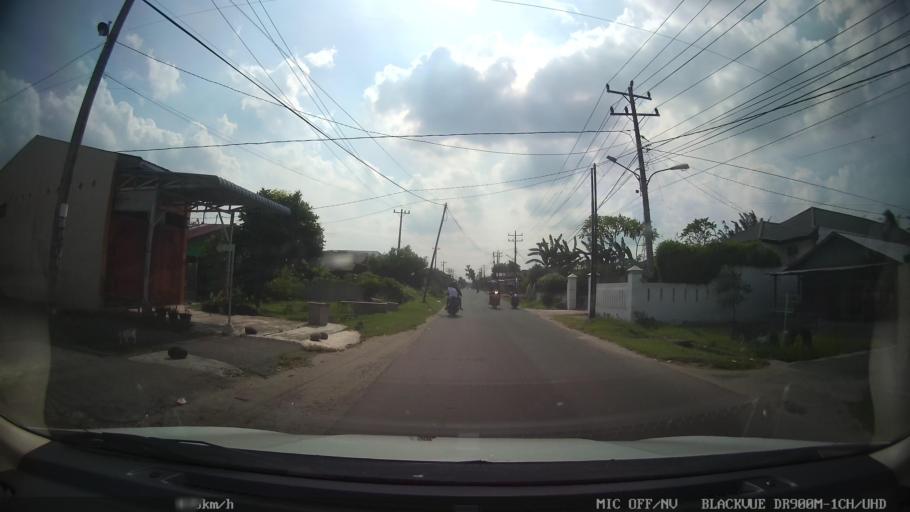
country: ID
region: North Sumatra
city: Binjai
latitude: 3.6437
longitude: 98.5099
